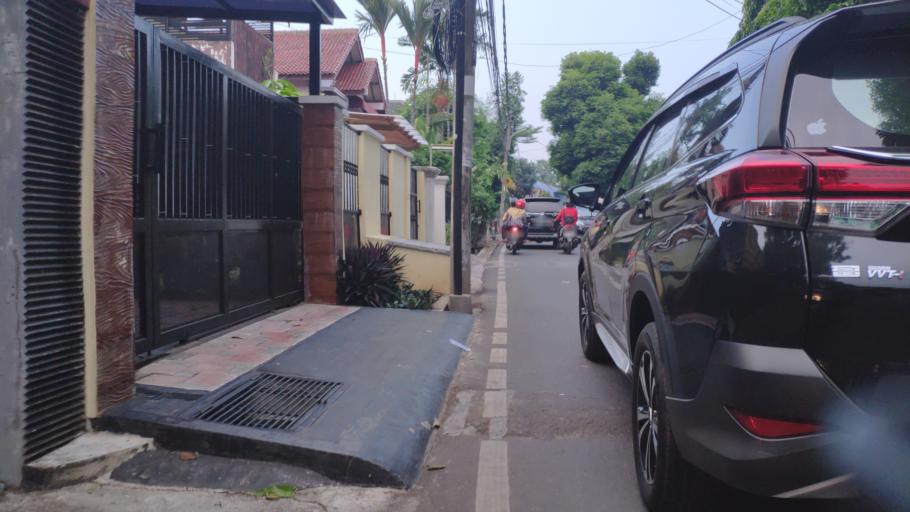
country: ID
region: West Java
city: Pamulang
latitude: -6.3049
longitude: 106.7988
